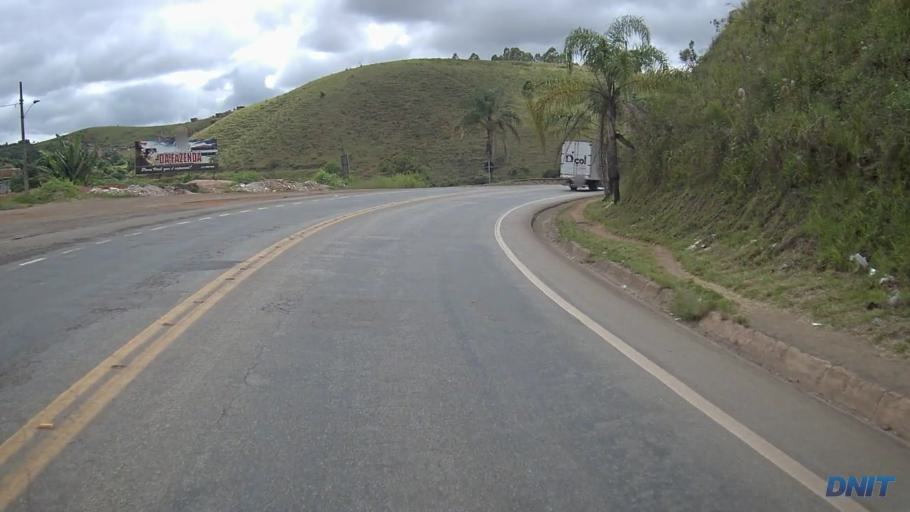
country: BR
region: Minas Gerais
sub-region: Joao Monlevade
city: Joao Monlevade
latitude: -19.8549
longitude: -43.2229
